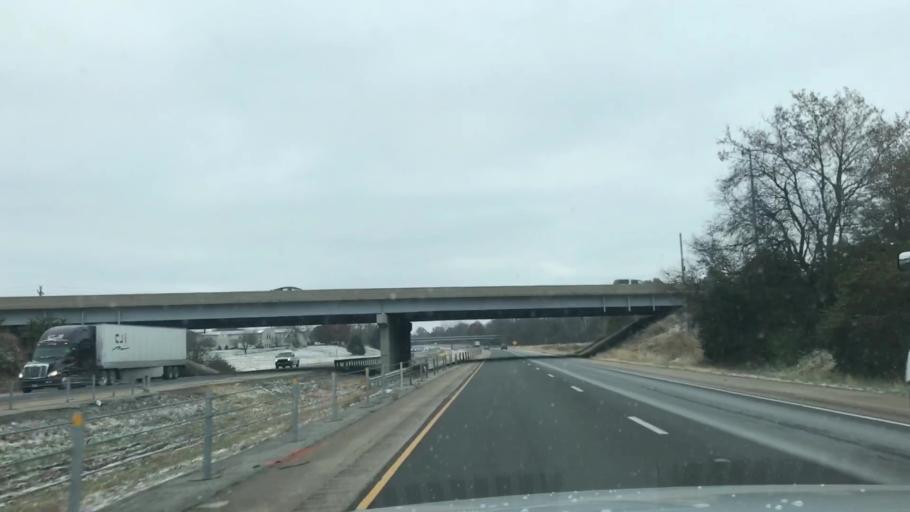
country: US
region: Illinois
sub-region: Madison County
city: Glen Carbon
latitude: 38.7561
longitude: -89.9575
